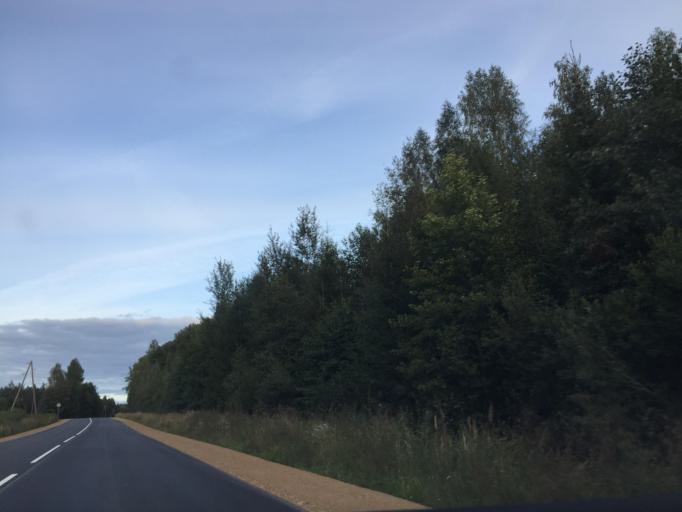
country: LV
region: Salas
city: Sala
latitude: 56.3959
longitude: 25.6978
